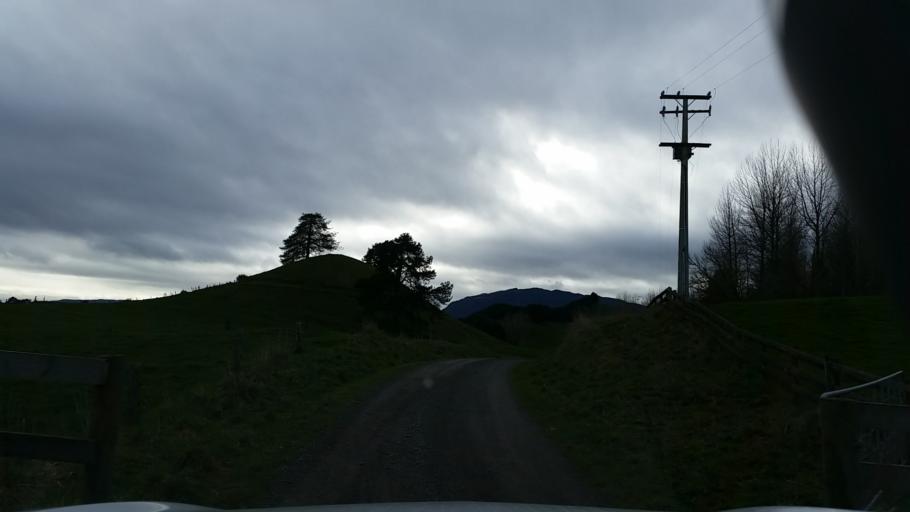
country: NZ
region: Bay of Plenty
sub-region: Rotorua District
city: Rotorua
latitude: -38.3027
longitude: 176.4191
